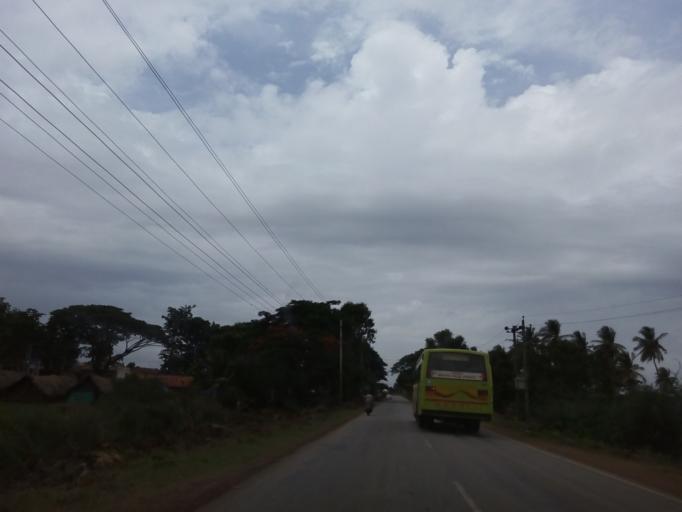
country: IN
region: Karnataka
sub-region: Davanagere
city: Harihar
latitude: 14.4960
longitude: 75.7804
